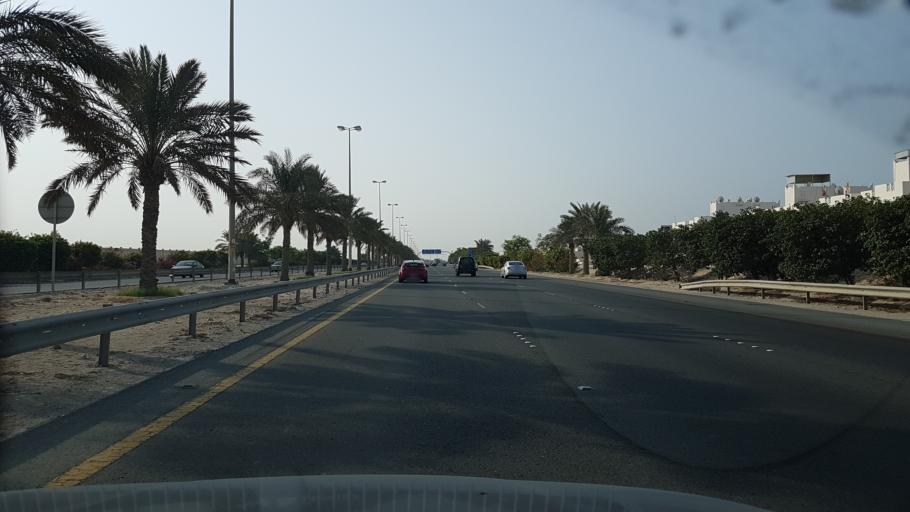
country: BH
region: Central Governorate
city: Madinat Hamad
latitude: 26.1107
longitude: 50.5111
